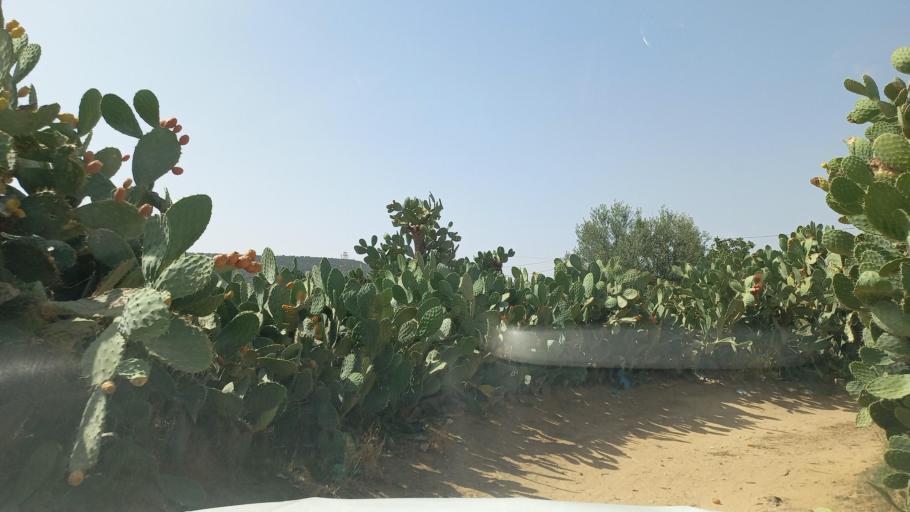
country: TN
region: Al Qasrayn
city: Sbiba
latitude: 35.3875
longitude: 8.9601
